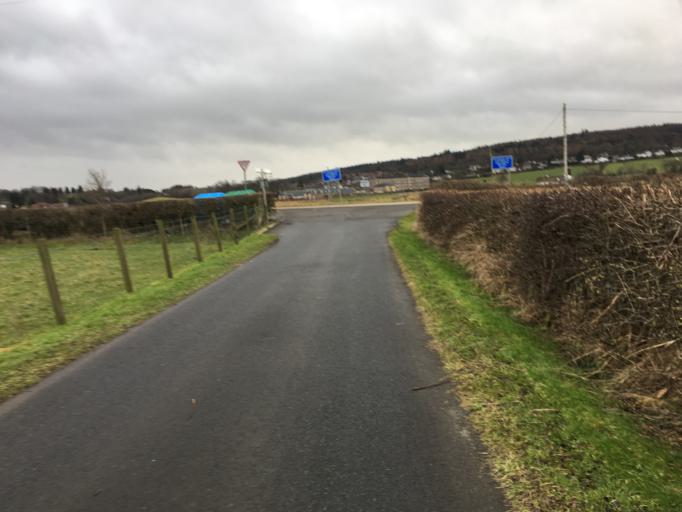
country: GB
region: Scotland
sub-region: Stirling
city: Stirling
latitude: 56.1191
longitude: -3.9742
